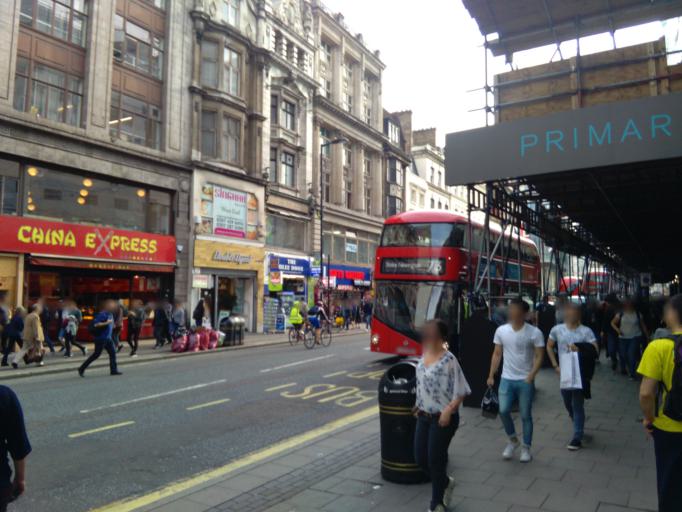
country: GB
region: England
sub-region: Greater London
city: London
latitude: 51.5164
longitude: -0.1311
